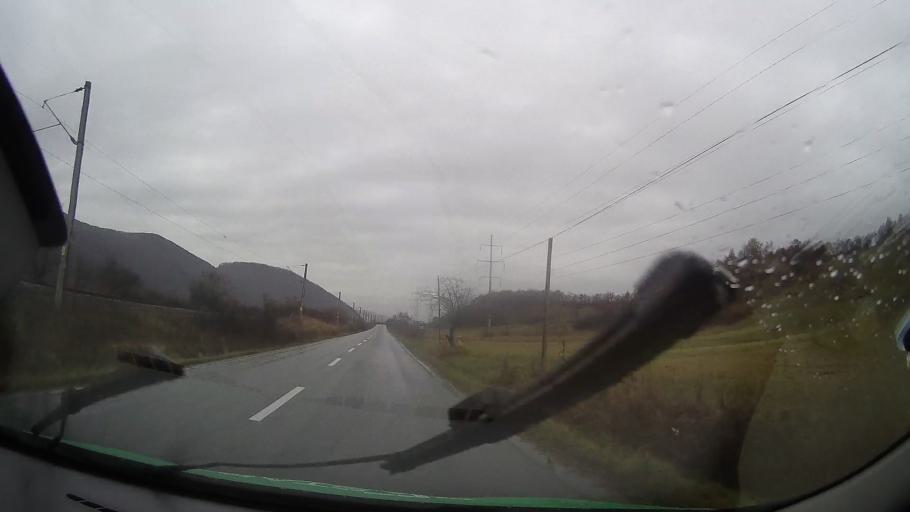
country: RO
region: Bistrita-Nasaud
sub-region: Municipiul Bistrita
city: Viisoara
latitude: 47.0491
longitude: 24.4576
